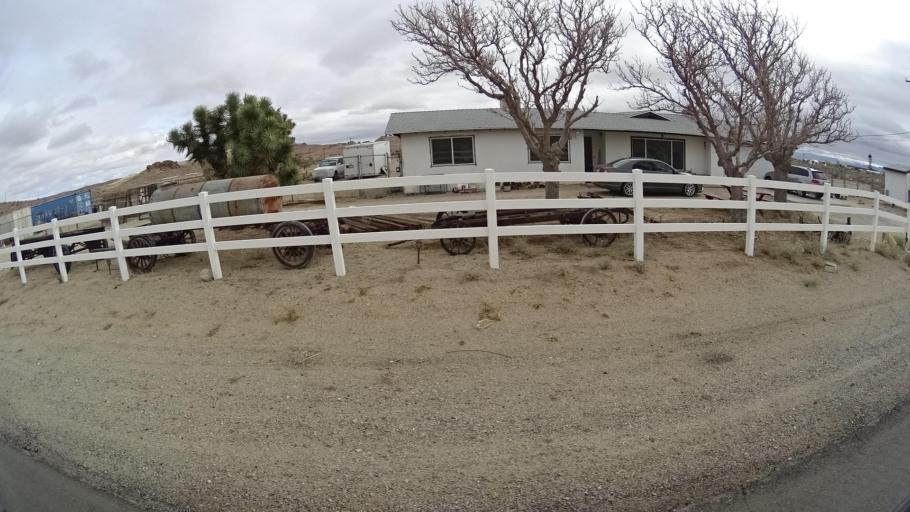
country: US
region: California
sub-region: Kern County
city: Rosamond
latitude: 34.8967
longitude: -118.2187
